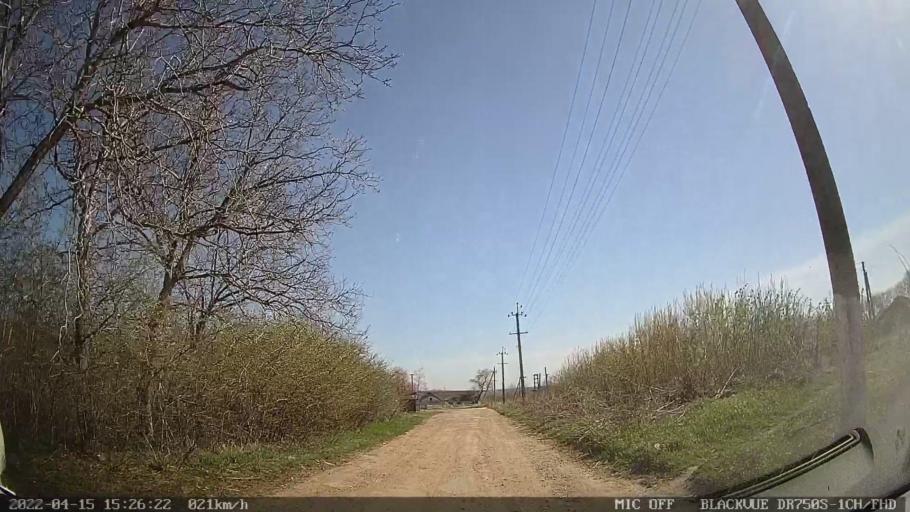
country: MD
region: Raionul Ocnita
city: Otaci
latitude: 48.3625
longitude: 27.9283
